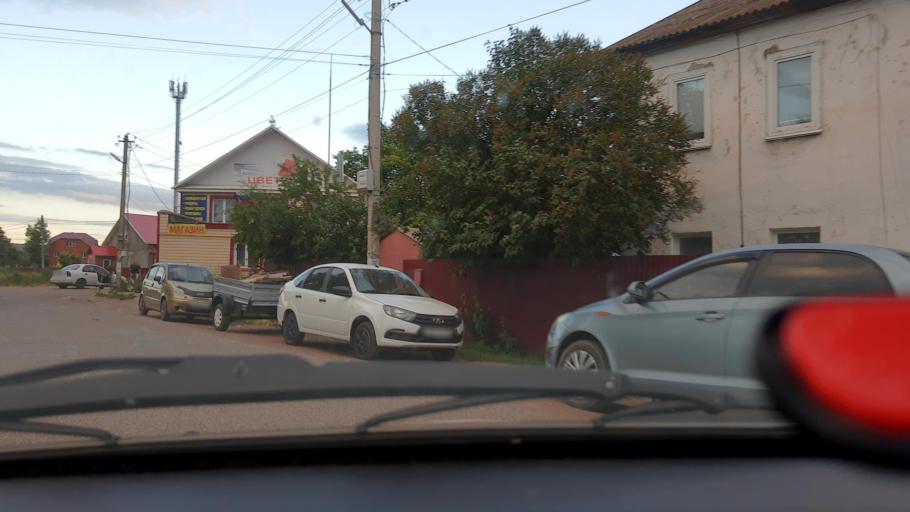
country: RU
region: Bashkortostan
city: Avdon
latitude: 54.4984
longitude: 55.8898
